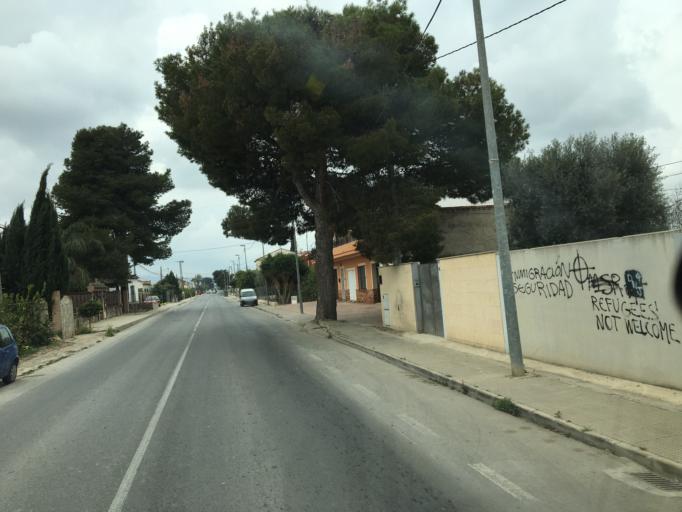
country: ES
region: Murcia
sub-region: Murcia
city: Beniel
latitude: 38.0275
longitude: -1.0272
